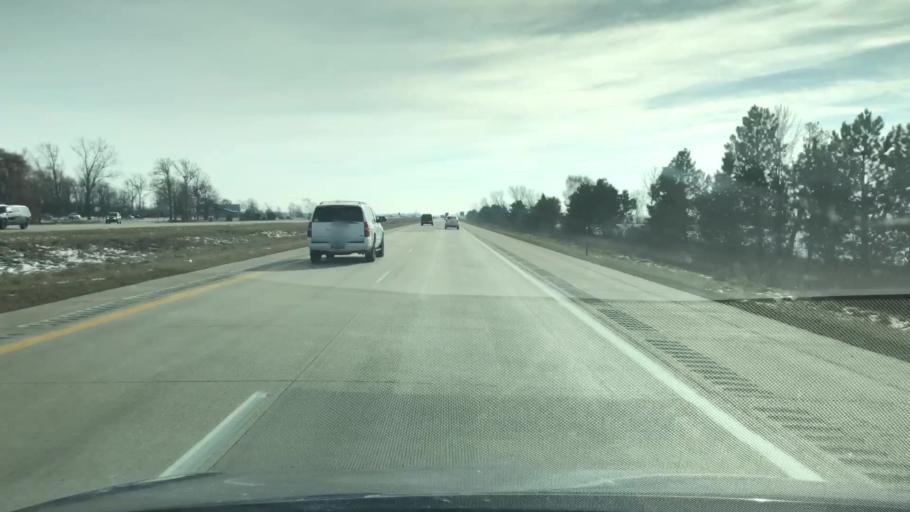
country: US
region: Michigan
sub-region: Bay County
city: Pinconning
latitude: 43.7652
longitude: -84.0209
